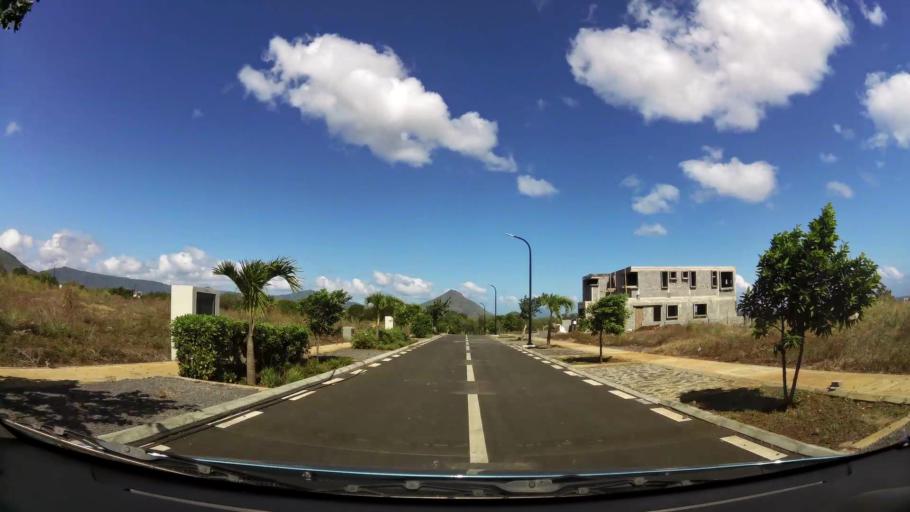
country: MU
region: Black River
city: Cascavelle
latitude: -20.2796
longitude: 57.3863
